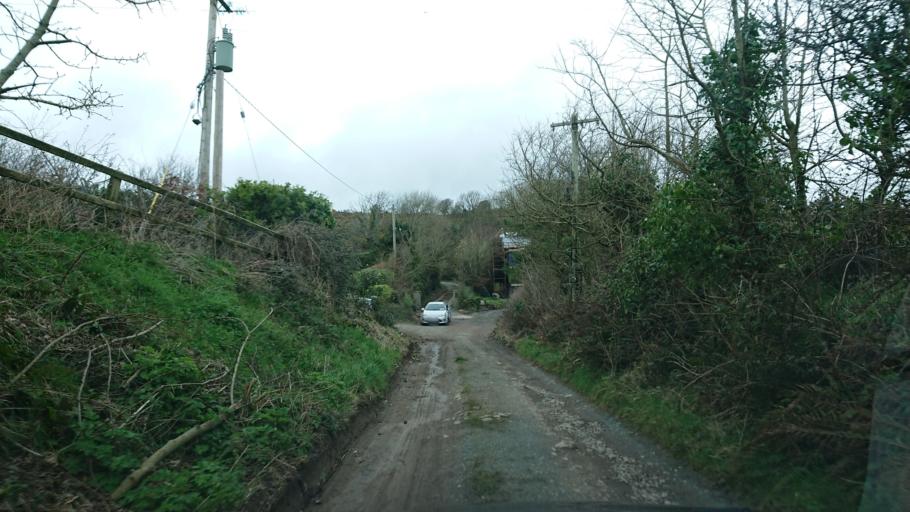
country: IE
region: Munster
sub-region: Waterford
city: Dunmore East
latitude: 52.1816
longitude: -6.9900
